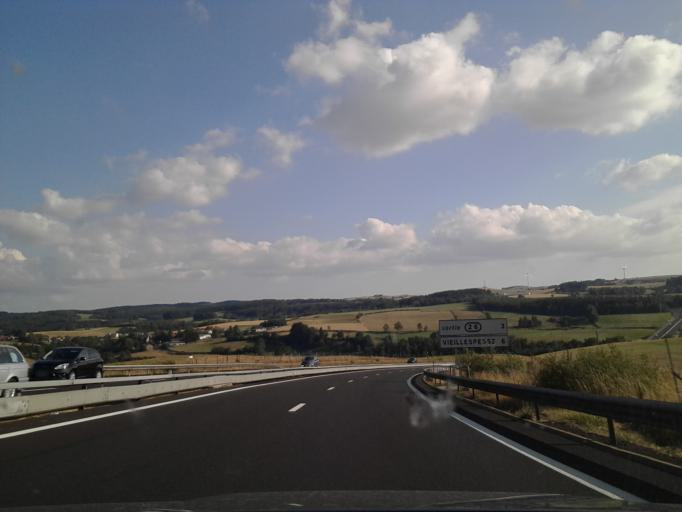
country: FR
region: Auvergne
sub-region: Departement du Cantal
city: Saint-Flour
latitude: 45.1406
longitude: 3.1443
